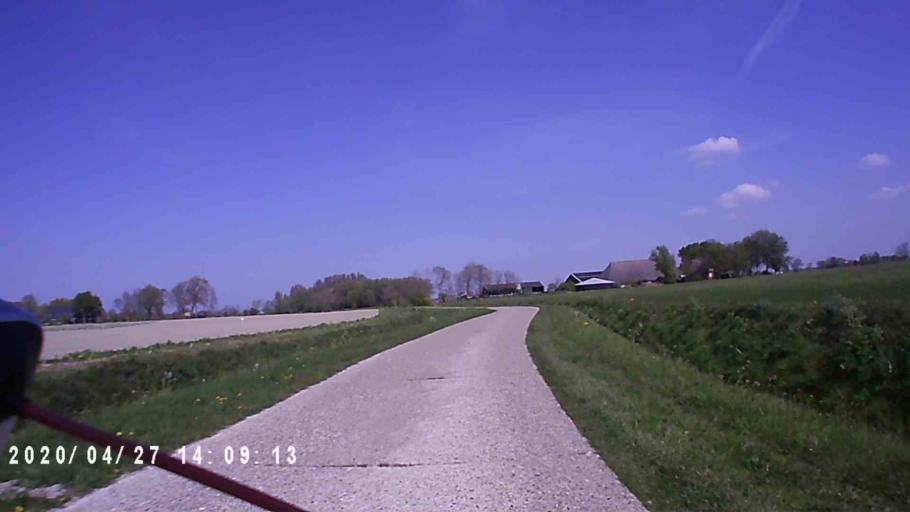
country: NL
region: Groningen
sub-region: Gemeente Zuidhorn
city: Oldehove
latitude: 53.3477
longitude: 6.3913
